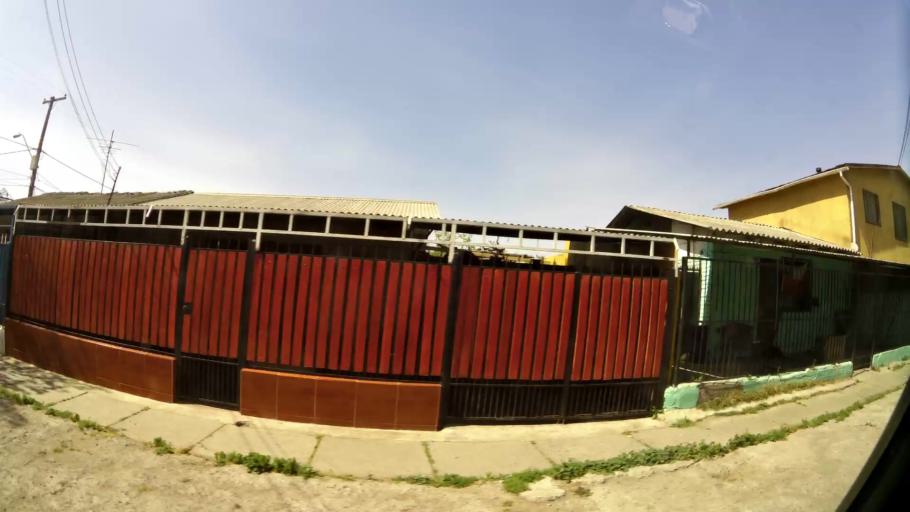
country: CL
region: Santiago Metropolitan
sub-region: Provincia de Maipo
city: San Bernardo
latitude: -33.5246
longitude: -70.7007
